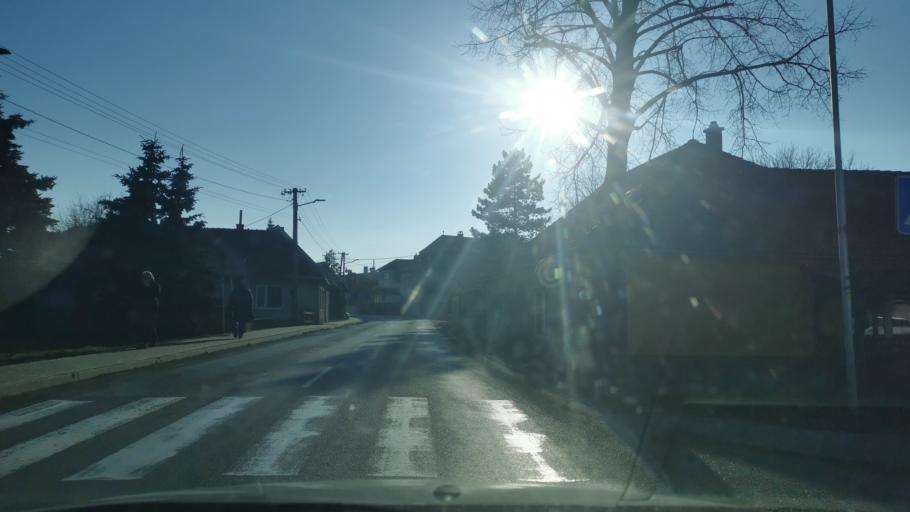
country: SK
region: Trnavsky
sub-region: Okres Senica
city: Senica
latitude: 48.7314
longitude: 17.4053
